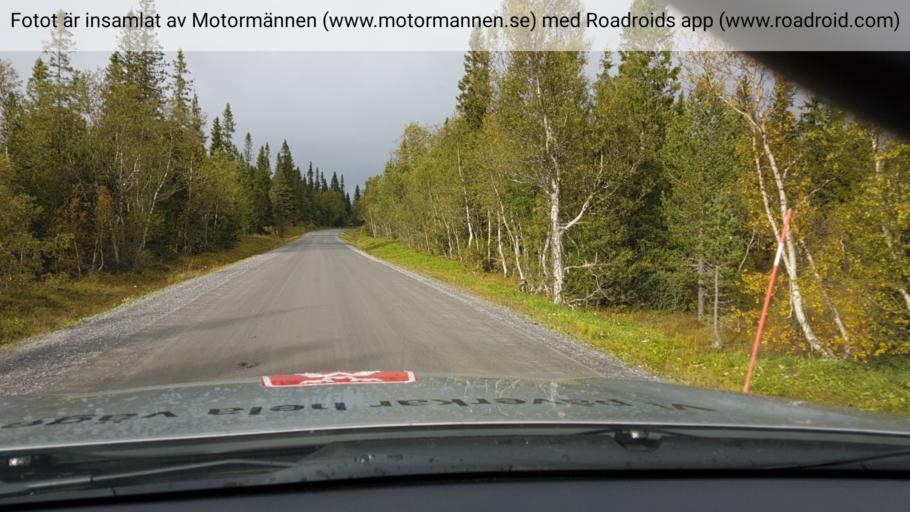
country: NO
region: Nord-Trondelag
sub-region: Snasa
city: Snaase
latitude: 63.7334
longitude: 12.4683
